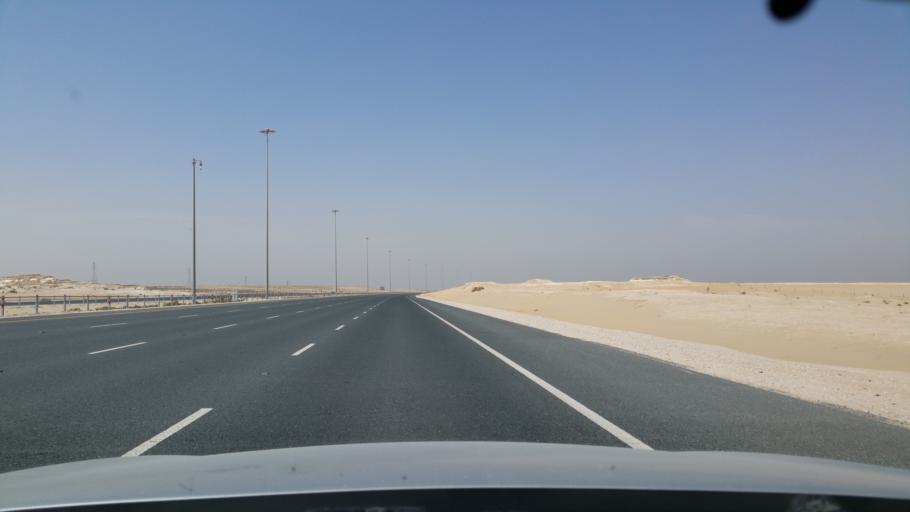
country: QA
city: Umm Bab
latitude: 24.8559
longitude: 50.8944
